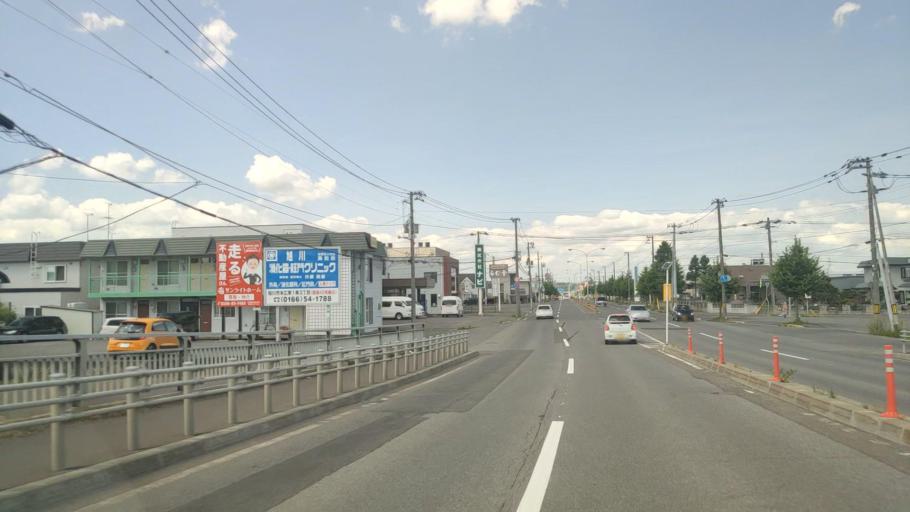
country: JP
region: Hokkaido
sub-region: Asahikawa-shi
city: Asahikawa
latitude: 43.7995
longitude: 142.3940
